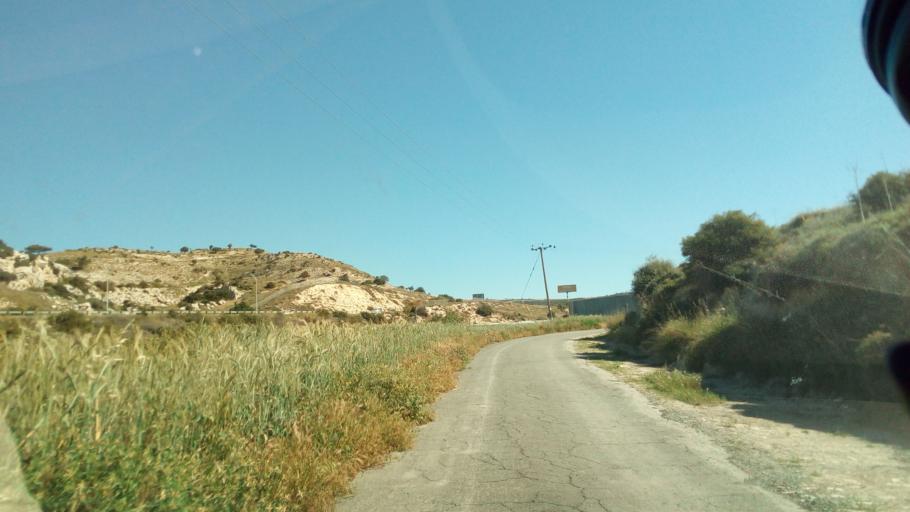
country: CY
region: Limassol
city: Pissouri
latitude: 34.6739
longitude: 32.6696
